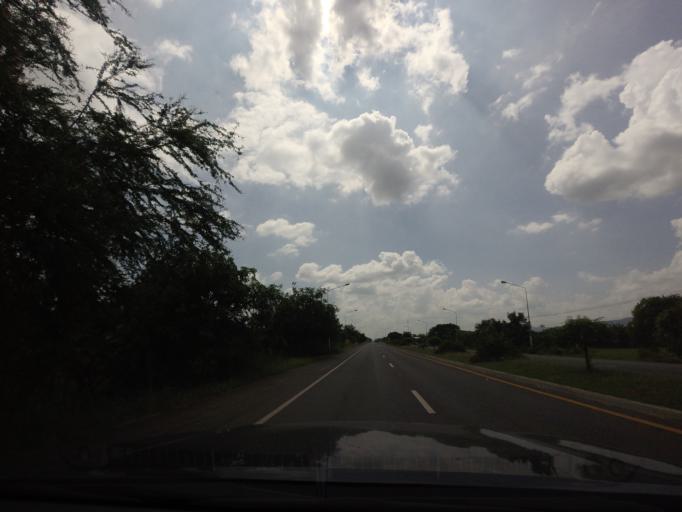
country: TH
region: Phetchabun
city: Nong Phai
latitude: 16.1679
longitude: 101.0753
